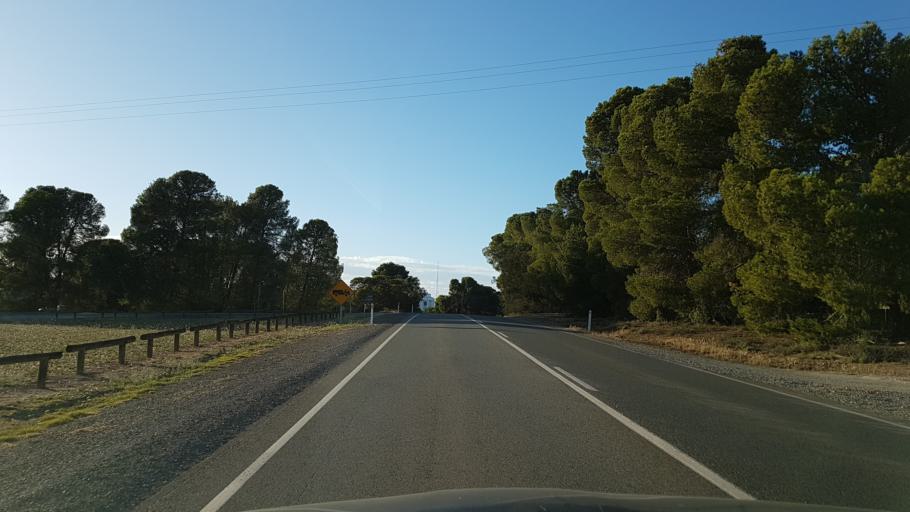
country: AU
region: South Australia
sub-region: Port Pirie City and Dists
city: Crystal Brook
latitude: -33.2691
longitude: 138.3506
